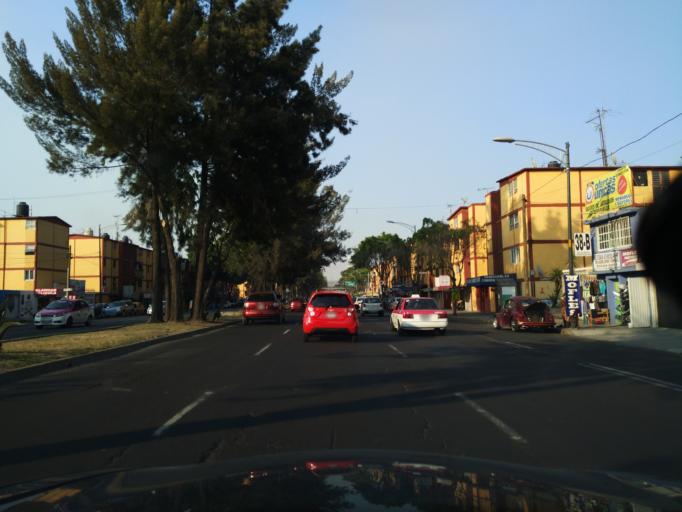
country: MX
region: Mexico City
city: Xochimilco
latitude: 19.3067
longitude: -99.1117
